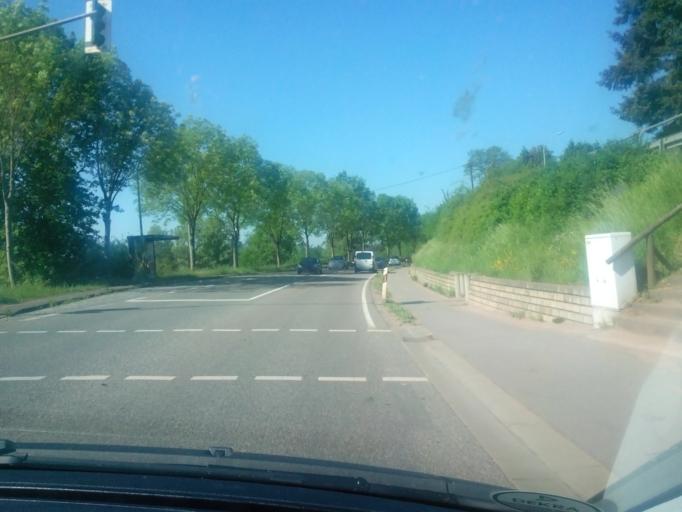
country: DE
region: Saarland
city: Nalbach
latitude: 49.3870
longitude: 6.8085
